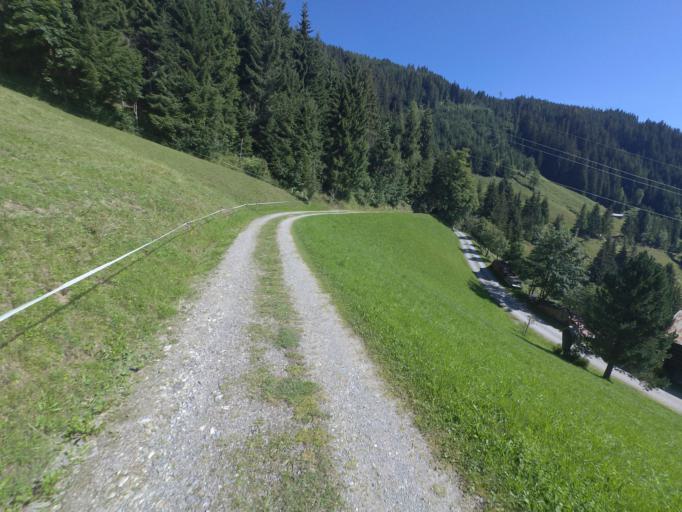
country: AT
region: Salzburg
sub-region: Politischer Bezirk Sankt Johann im Pongau
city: Muhlbach am Hochkonig
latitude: 47.3618
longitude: 13.1555
